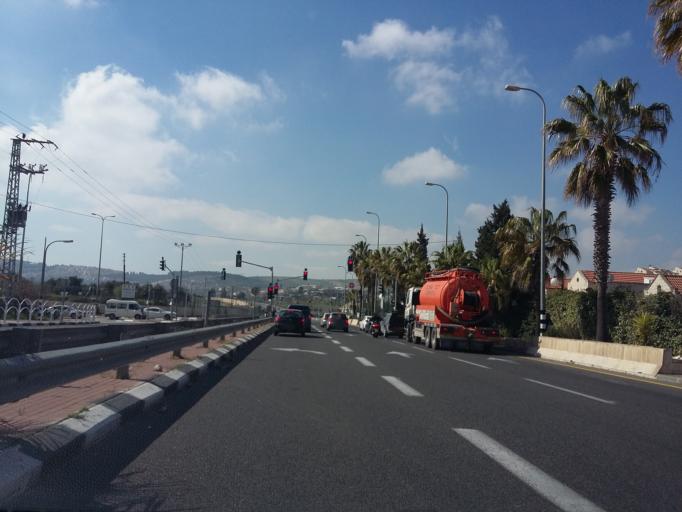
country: IL
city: Givat Zeev
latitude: 31.8587
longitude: 35.1742
